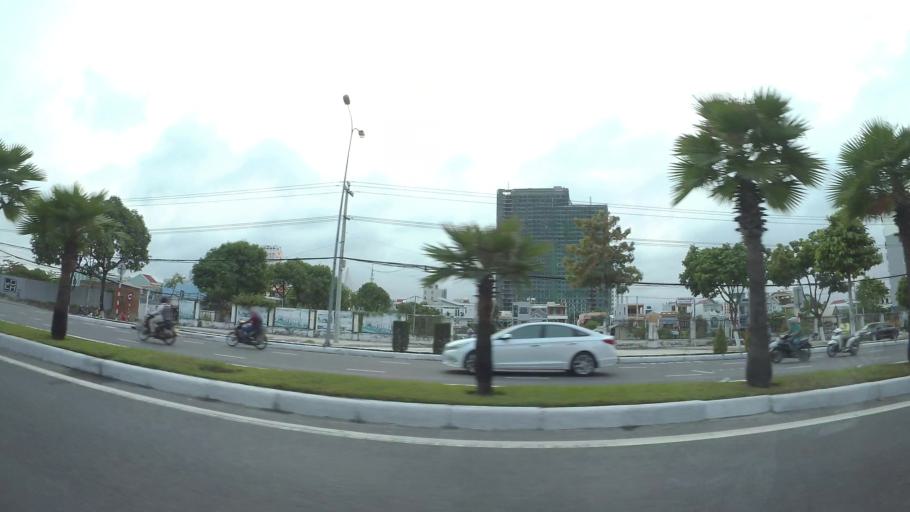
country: VN
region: Da Nang
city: Son Tra
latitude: 16.0555
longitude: 108.2362
